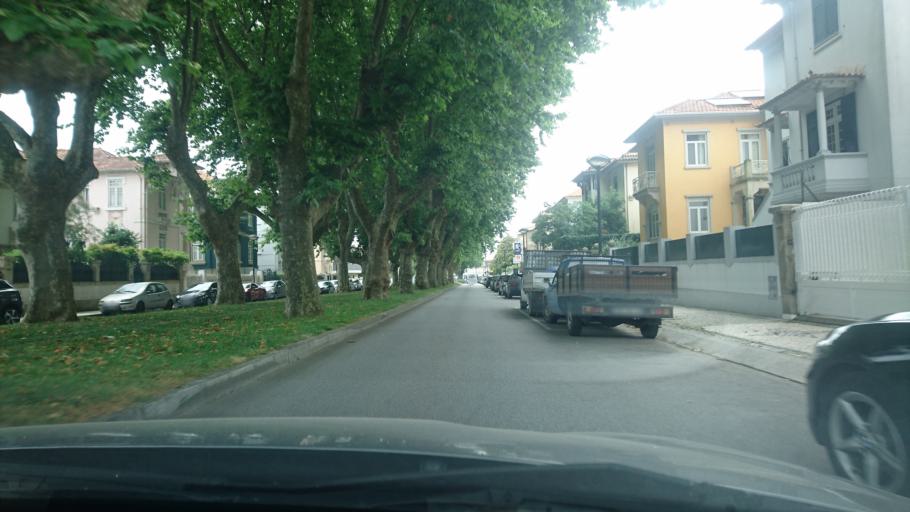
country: PT
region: Porto
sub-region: Porto
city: Porto
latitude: 41.1652
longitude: -8.5959
